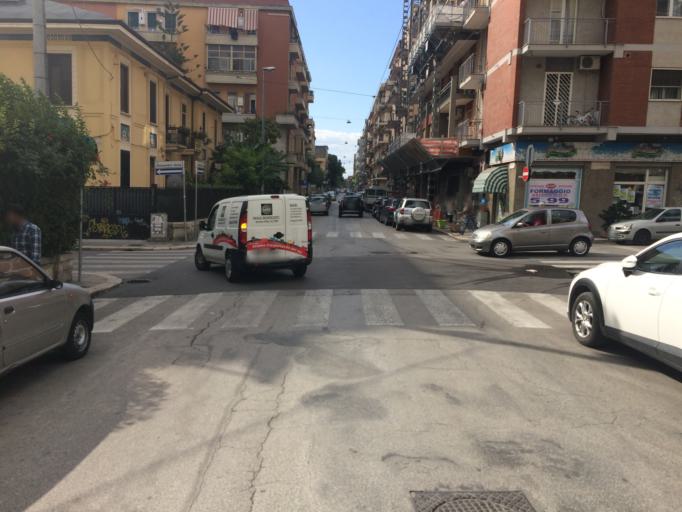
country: IT
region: Apulia
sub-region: Provincia di Bari
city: Bari
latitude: 41.1127
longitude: 16.8723
